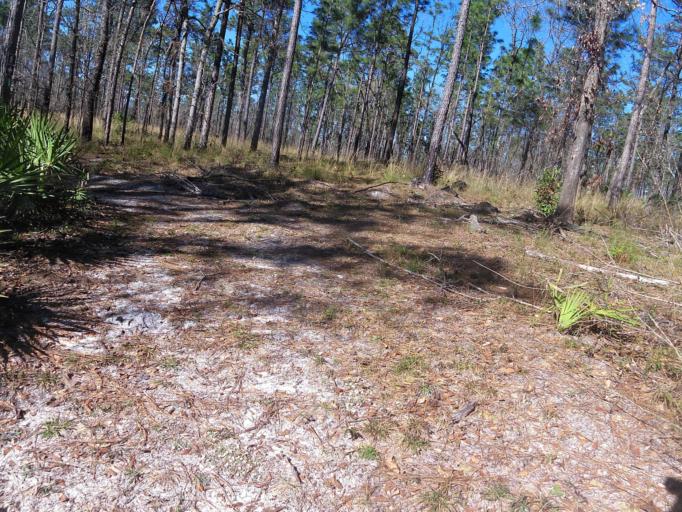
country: US
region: Florida
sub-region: Clay County
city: Middleburg
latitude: 30.1383
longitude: -81.8903
